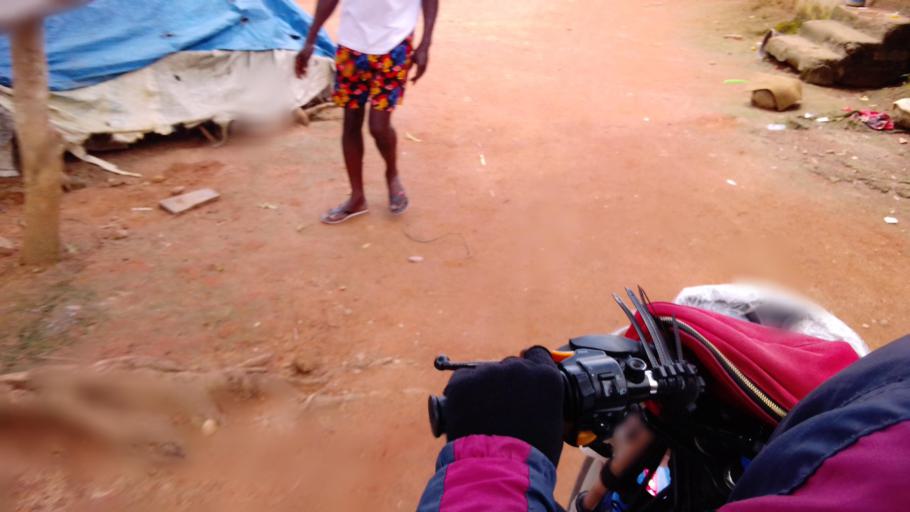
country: SL
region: Eastern Province
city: Koyima
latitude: 8.6753
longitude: -10.9969
